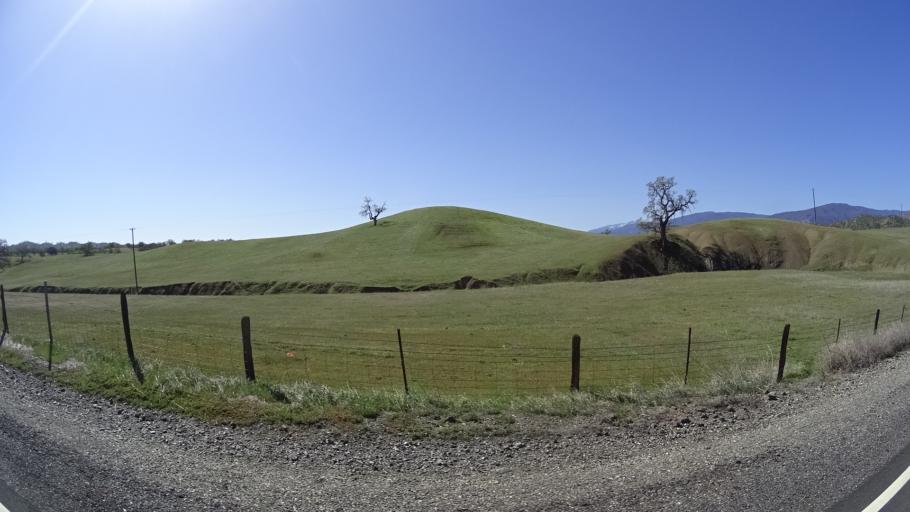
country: US
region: California
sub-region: Glenn County
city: Orland
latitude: 39.6596
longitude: -122.5457
